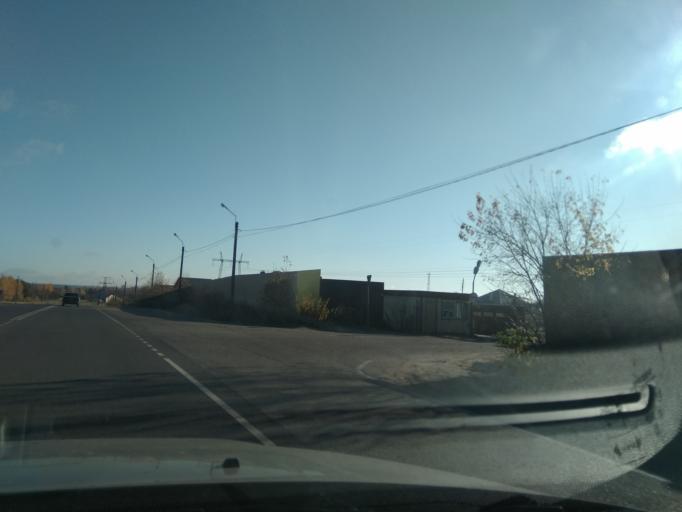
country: RU
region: Moskovskaya
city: Istra
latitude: 55.8796
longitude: 36.8363
